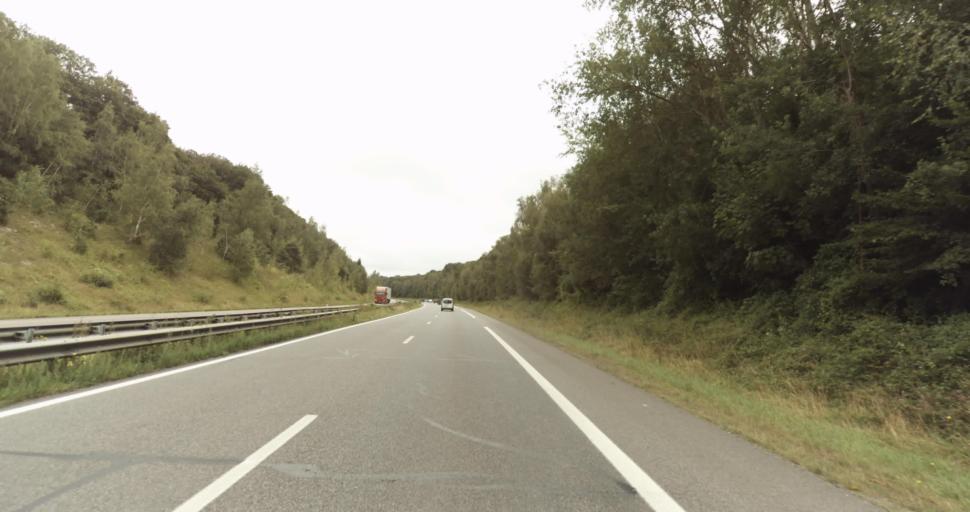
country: FR
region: Haute-Normandie
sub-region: Departement de l'Eure
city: Heudreville-sur-Eure
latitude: 49.1121
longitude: 1.1874
